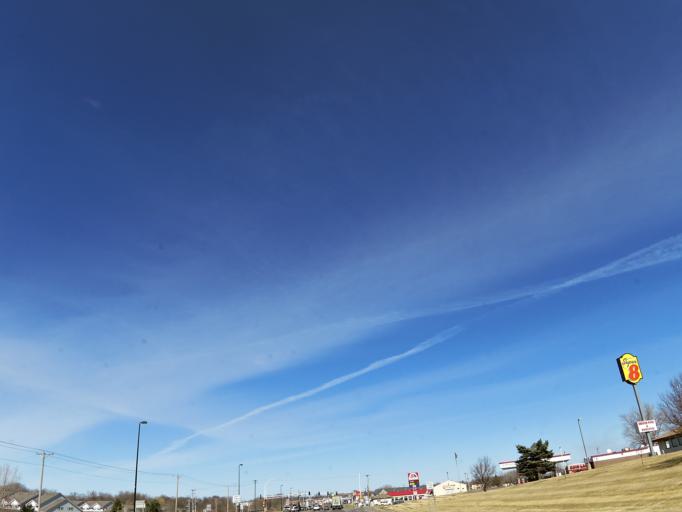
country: US
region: Minnesota
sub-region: Wright County
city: Buffalo
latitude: 45.1670
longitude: -93.8594
